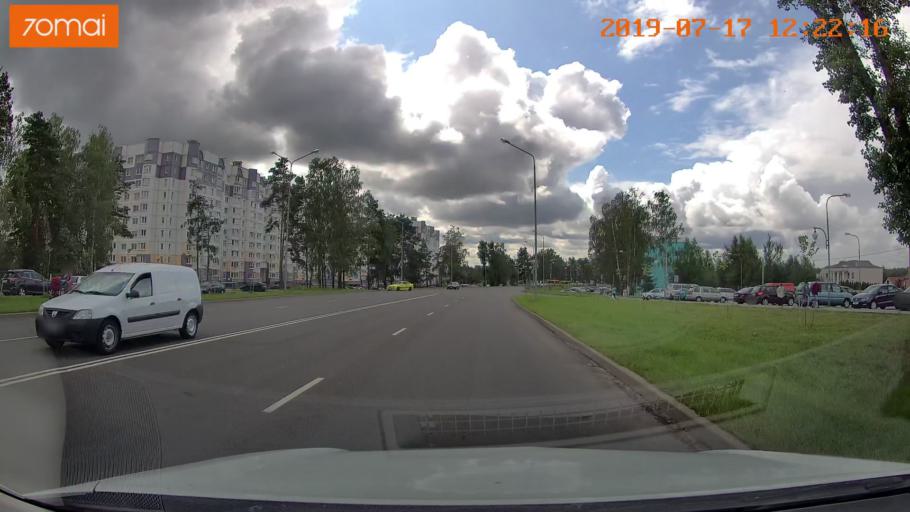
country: BY
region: Minsk
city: Borovlyany
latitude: 54.0025
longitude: 27.6777
